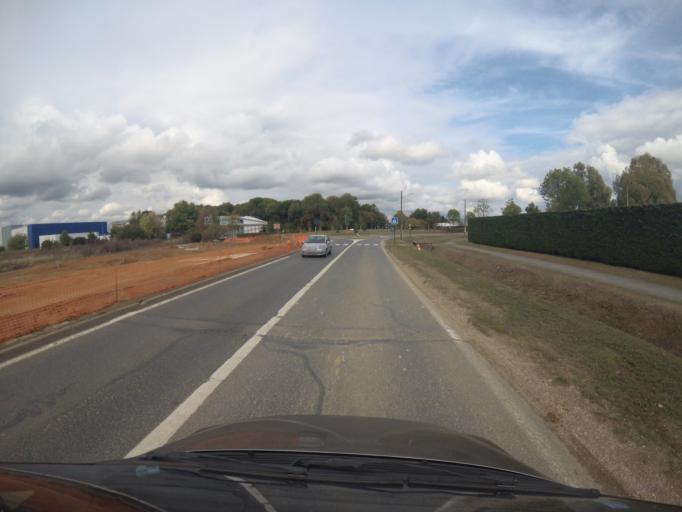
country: FR
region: Ile-de-France
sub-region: Departement de Seine-et-Marne
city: Montevrain
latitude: 48.8653
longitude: 2.7649
